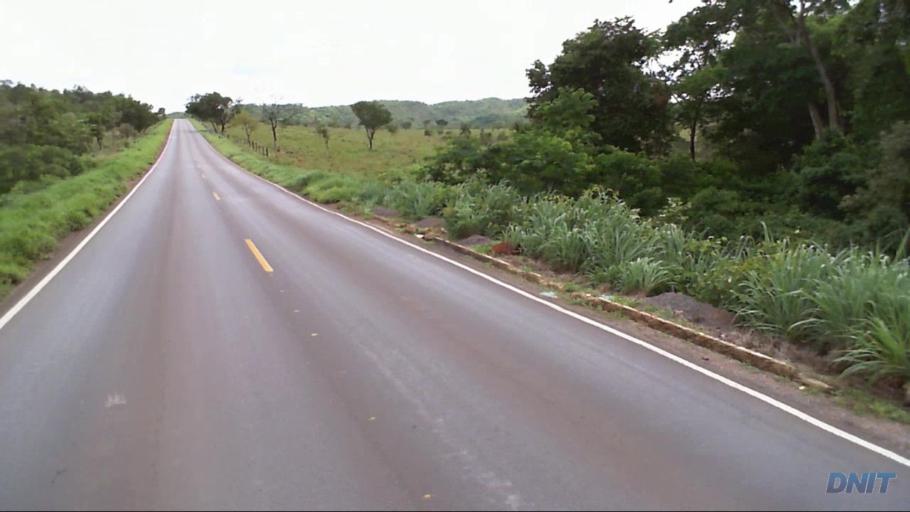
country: BR
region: Goias
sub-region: Padre Bernardo
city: Padre Bernardo
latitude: -15.4429
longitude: -48.1990
